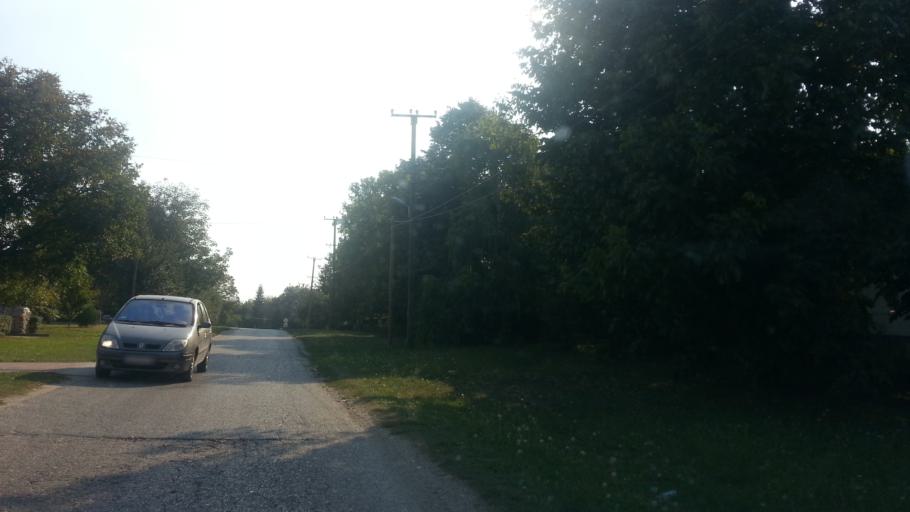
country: RS
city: Stari Banovci
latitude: 44.9831
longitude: 20.2732
